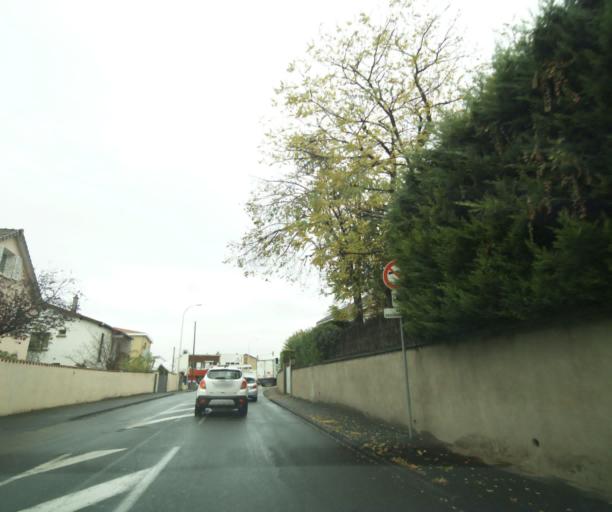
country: FR
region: Auvergne
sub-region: Departement du Puy-de-Dome
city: Cournon-d'Auvergne
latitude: 45.7398
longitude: 3.1938
